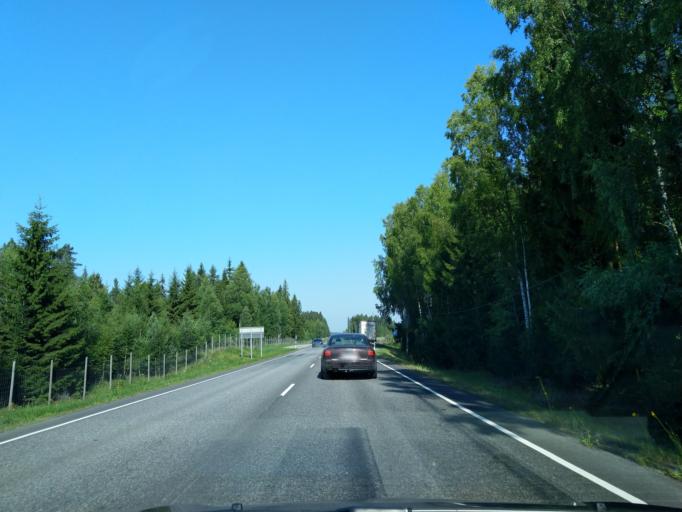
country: FI
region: Pirkanmaa
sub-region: Lounais-Pirkanmaa
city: Punkalaidun
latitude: 61.0260
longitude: 23.0376
